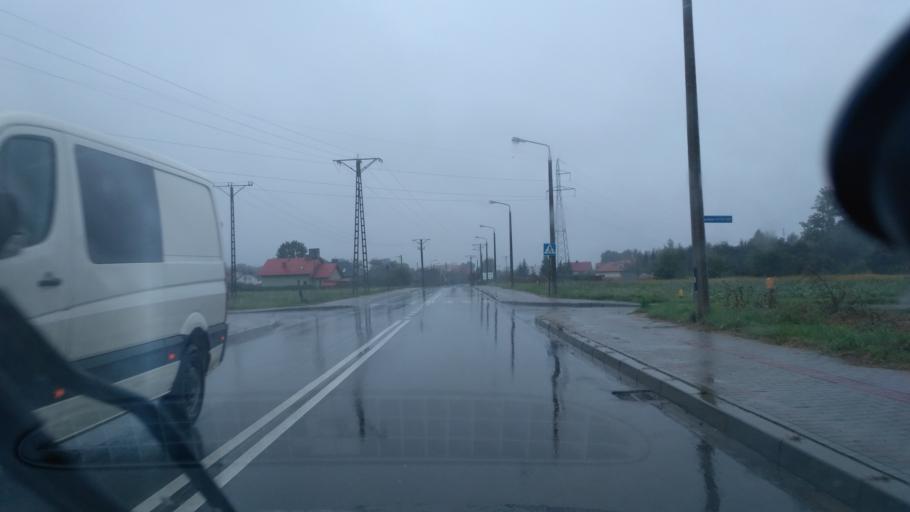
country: PL
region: Subcarpathian Voivodeship
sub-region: Powiat debicki
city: Debica
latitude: 50.0662
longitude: 21.4168
